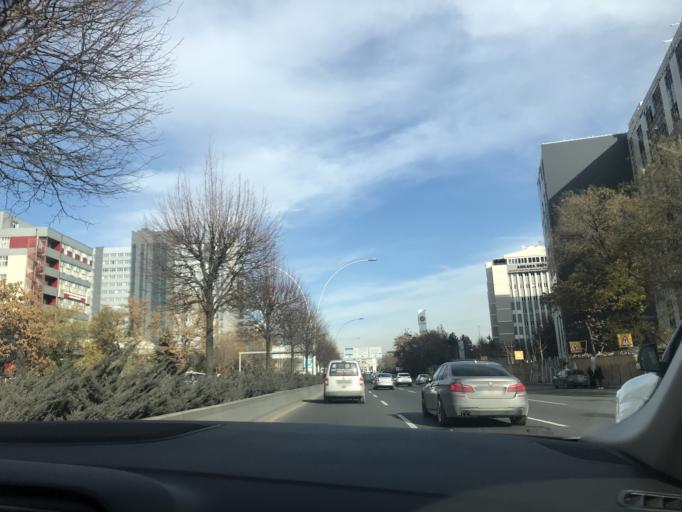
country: TR
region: Ankara
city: Ankara
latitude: 39.9376
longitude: 32.8242
